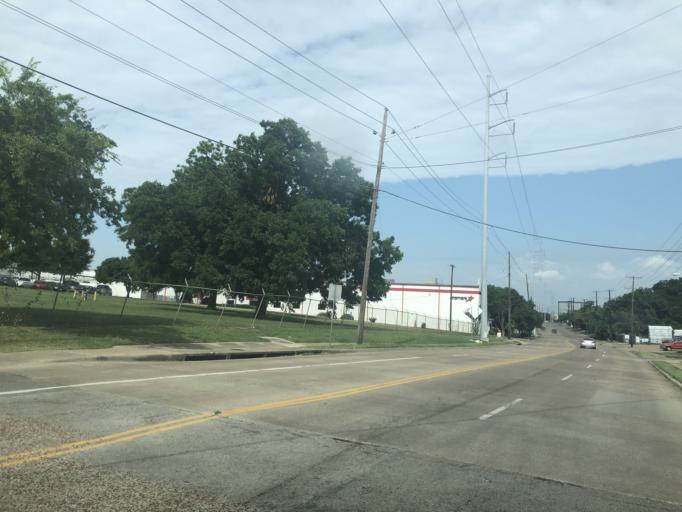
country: US
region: Texas
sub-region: Dallas County
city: University Park
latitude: 32.8262
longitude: -96.8555
